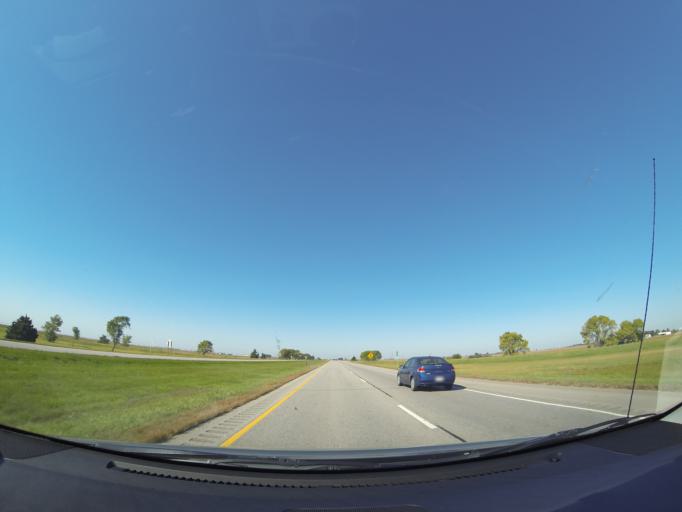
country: US
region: Nebraska
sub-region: Seward County
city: Seward
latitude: 40.8227
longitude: -97.2177
